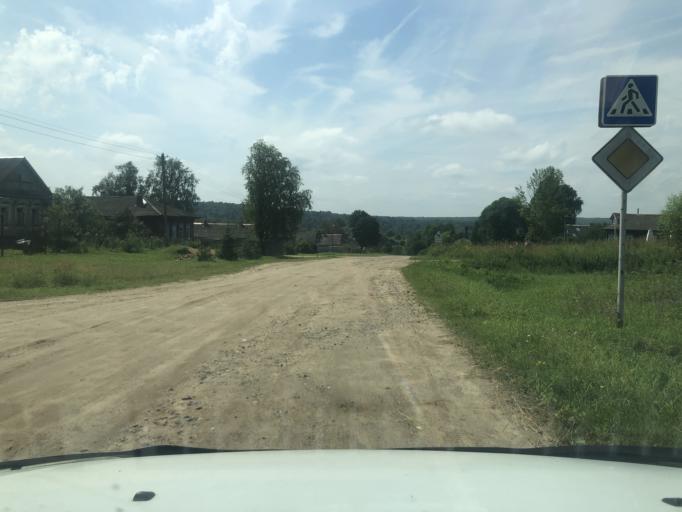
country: RU
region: Jaroslavl
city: Pereslavl'-Zalesskiy
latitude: 57.0447
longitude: 38.8639
